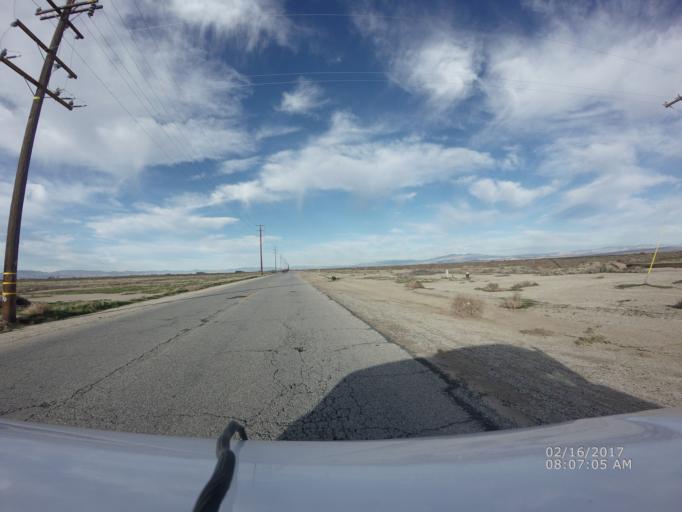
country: US
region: California
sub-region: Kern County
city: Edwards Air Force Base
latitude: 34.7638
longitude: -117.9785
